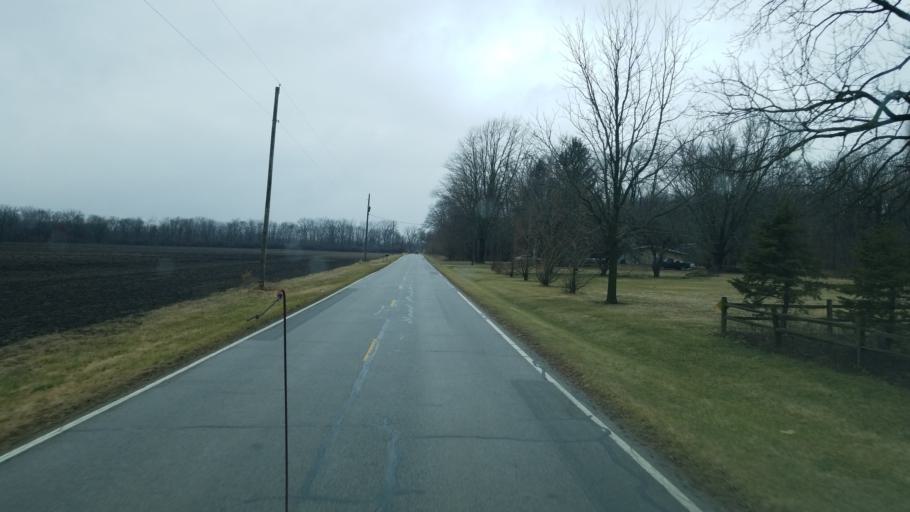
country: US
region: Ohio
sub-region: Marion County
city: Marion
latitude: 40.6222
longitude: -83.1677
